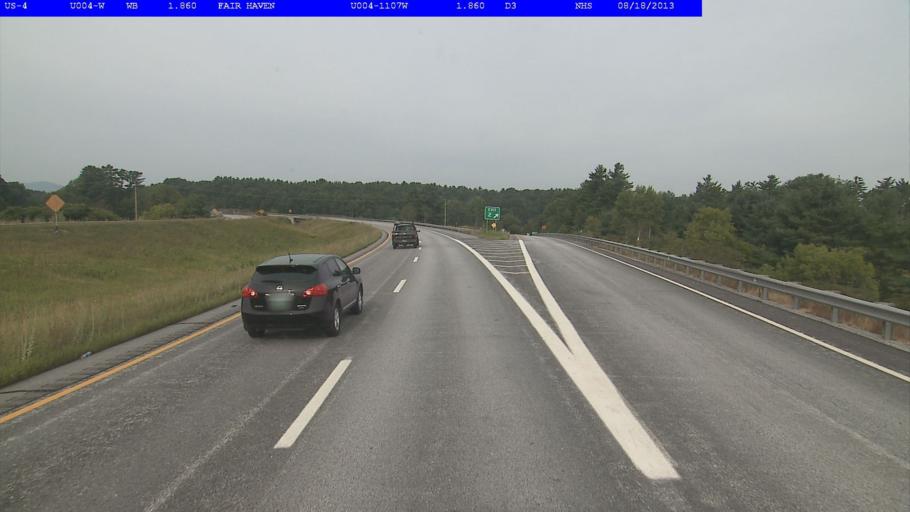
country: US
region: Vermont
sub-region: Rutland County
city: Fair Haven
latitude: 43.6064
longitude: -73.2744
